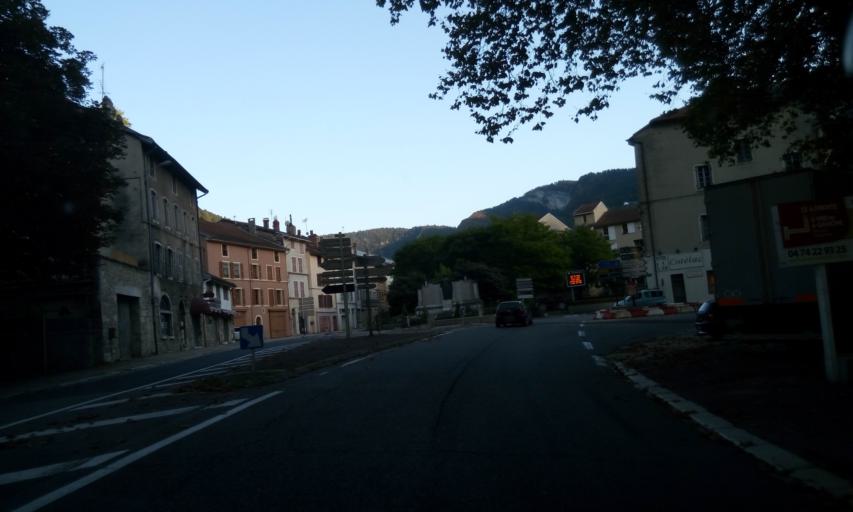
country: FR
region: Rhone-Alpes
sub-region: Departement de l'Ain
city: Nantua
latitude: 46.1570
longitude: 5.6043
